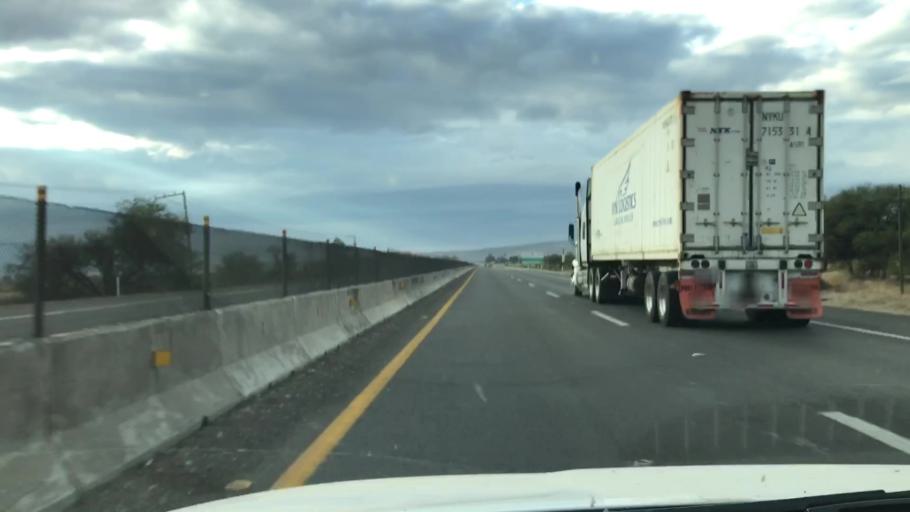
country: MX
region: Guanajuato
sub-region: Penjamo
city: Mezquite de Luna
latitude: 20.3851
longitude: -101.9075
